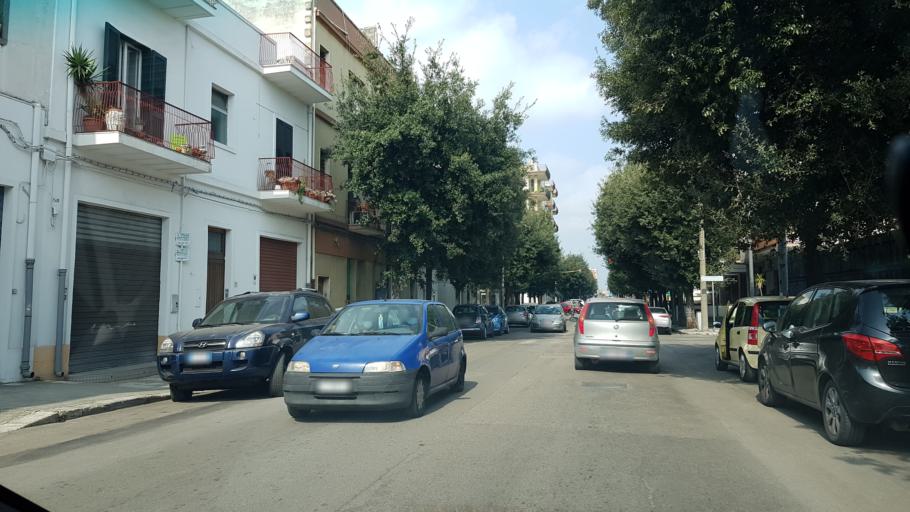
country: IT
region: Apulia
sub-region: Provincia di Lecce
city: Castromediano
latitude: 40.3385
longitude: 18.1773
